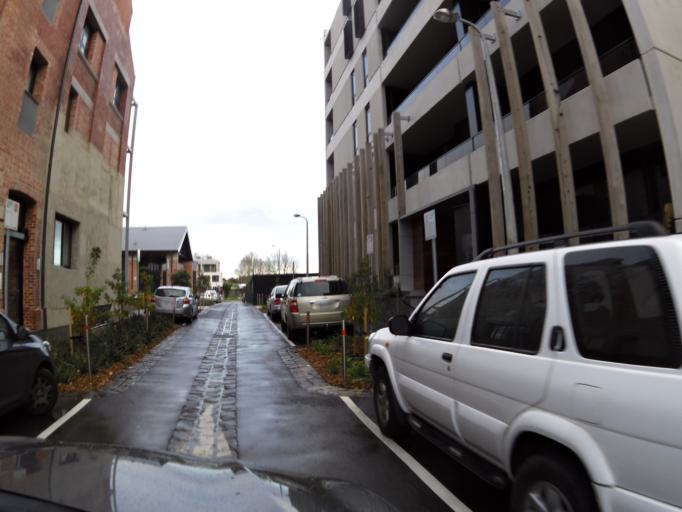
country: AU
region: Victoria
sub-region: Yarra
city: Richmond
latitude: -37.8242
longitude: 145.0112
